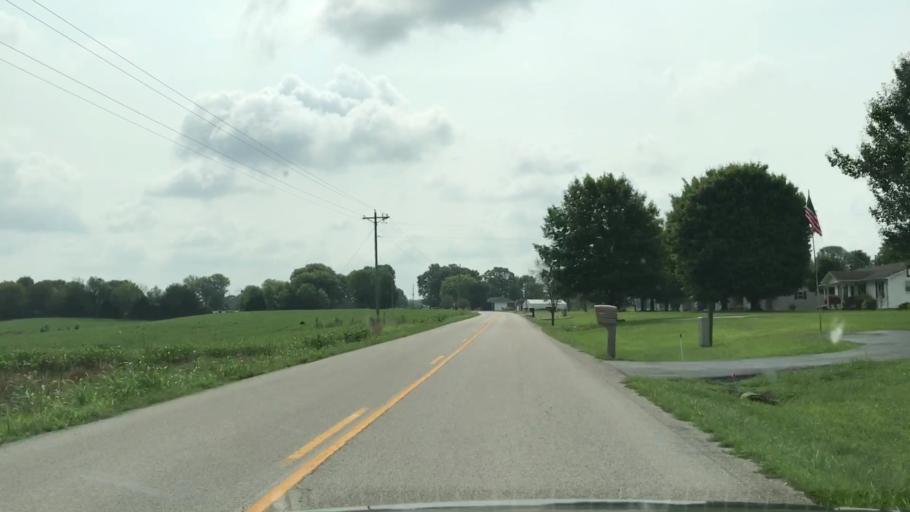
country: US
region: Kentucky
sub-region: Edmonson County
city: Brownsville
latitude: 37.1353
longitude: -86.1747
